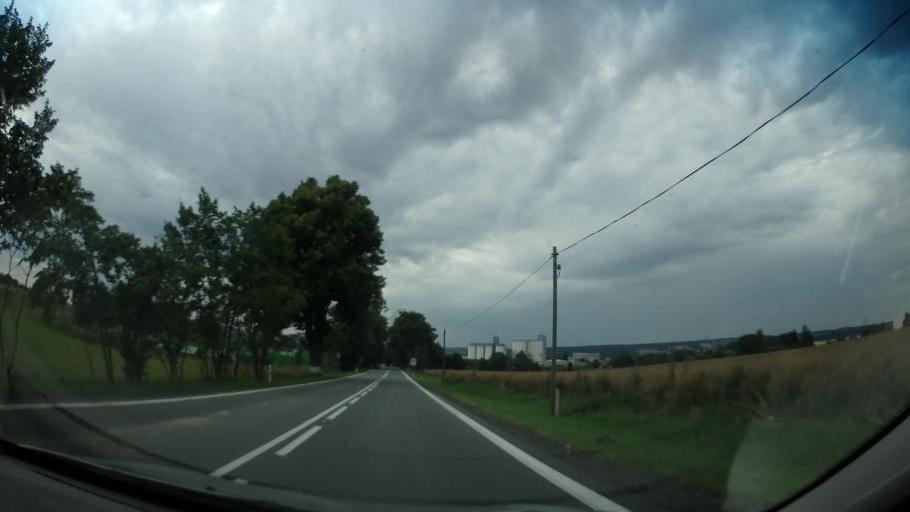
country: CZ
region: Pardubicky
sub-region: Okres Svitavy
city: Svitavy
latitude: 49.7595
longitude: 16.4918
